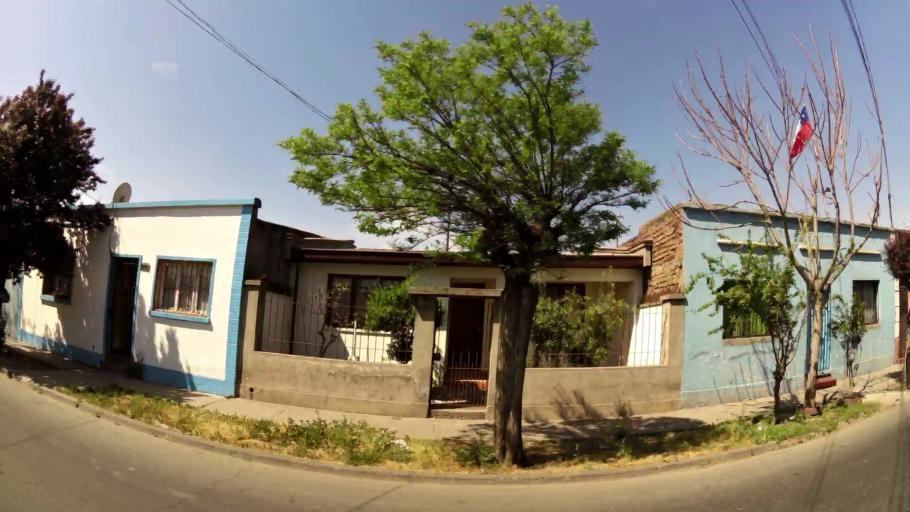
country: CL
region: Santiago Metropolitan
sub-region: Provincia de Santiago
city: La Pintana
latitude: -33.5313
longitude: -70.6488
